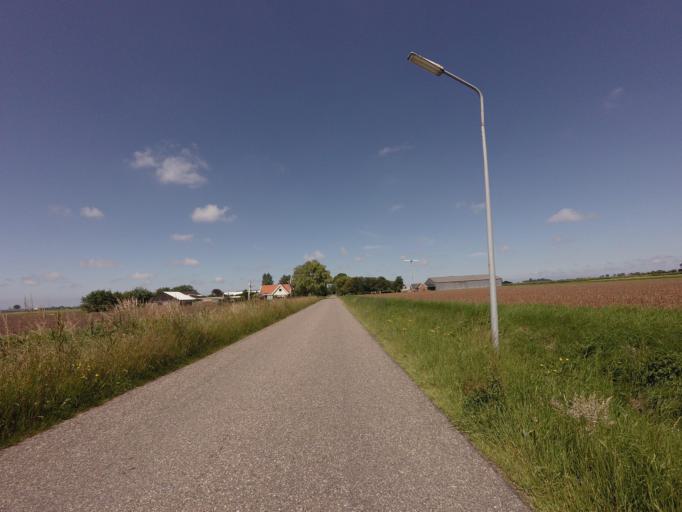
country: NL
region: North Holland
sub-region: Gemeente Schagen
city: Schagen
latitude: 52.8811
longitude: 4.8406
